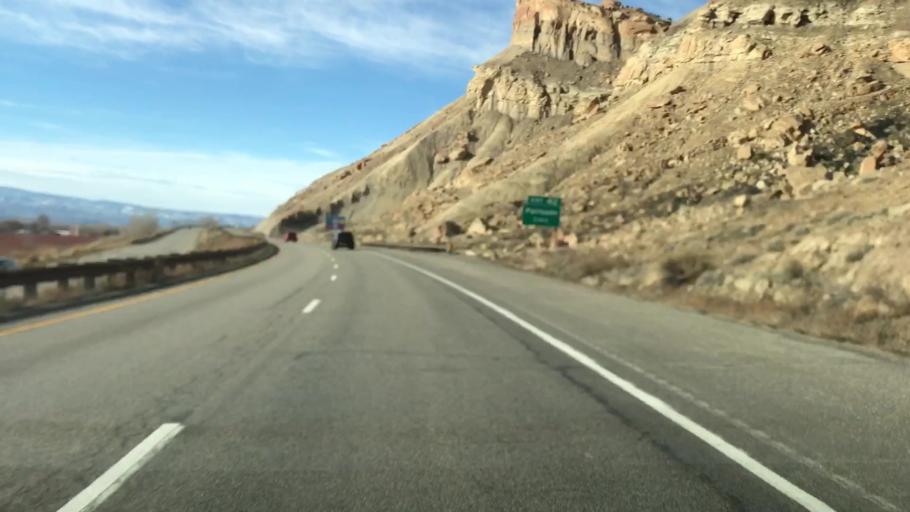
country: US
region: Colorado
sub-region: Mesa County
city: Palisade
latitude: 39.1194
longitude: -108.3400
